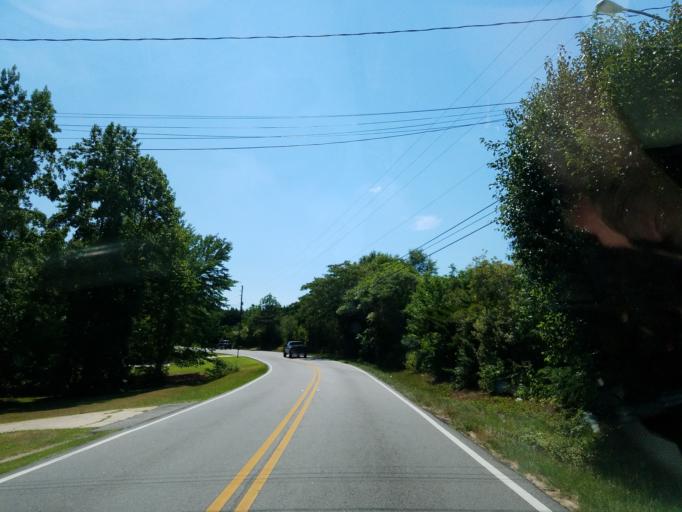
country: US
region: Georgia
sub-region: Henry County
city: Stockbridge
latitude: 33.4790
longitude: -84.2465
